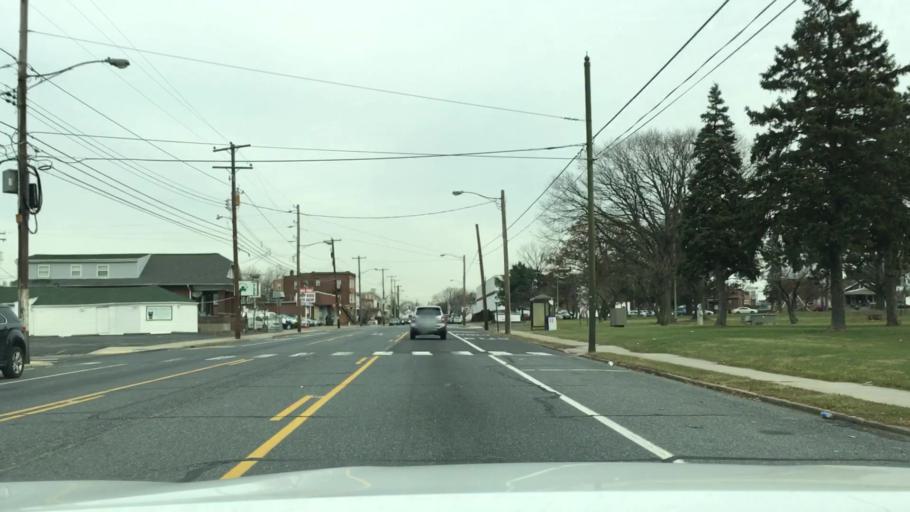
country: US
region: Pennsylvania
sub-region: Lehigh County
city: Fountain Hill
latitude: 40.6192
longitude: -75.4318
